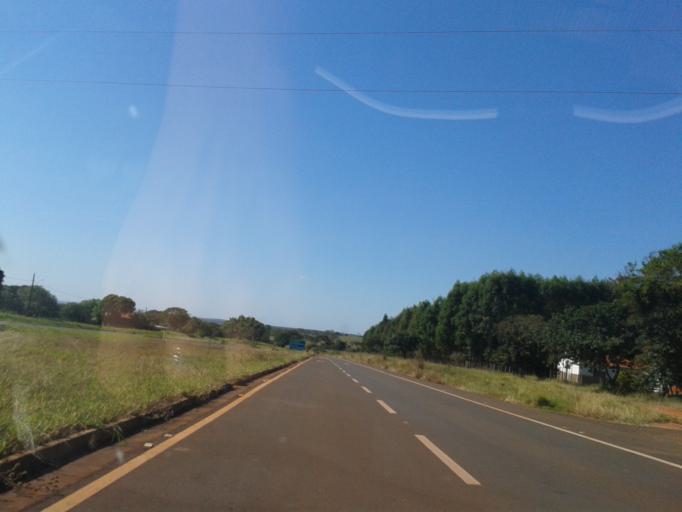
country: BR
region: Minas Gerais
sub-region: Campina Verde
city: Campina Verde
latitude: -19.3299
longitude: -49.6448
